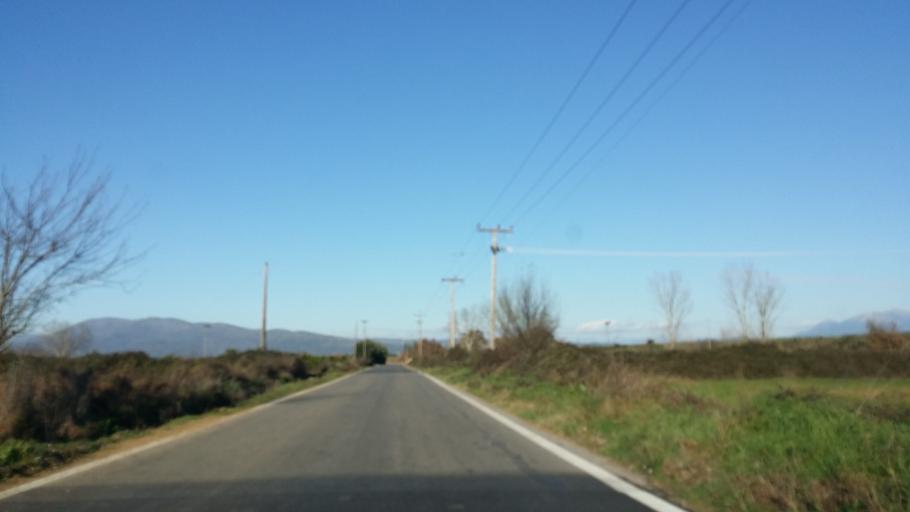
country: GR
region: West Greece
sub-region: Nomos Aitolias kai Akarnanias
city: Angelokastro
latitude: 38.6199
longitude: 21.2283
